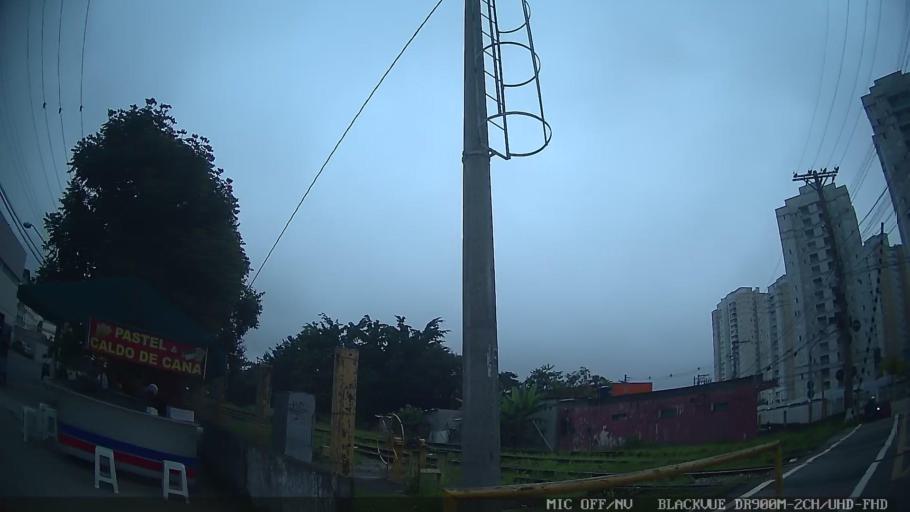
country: BR
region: Sao Paulo
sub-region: Mogi das Cruzes
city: Mogi das Cruzes
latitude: -23.5052
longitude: -46.1519
